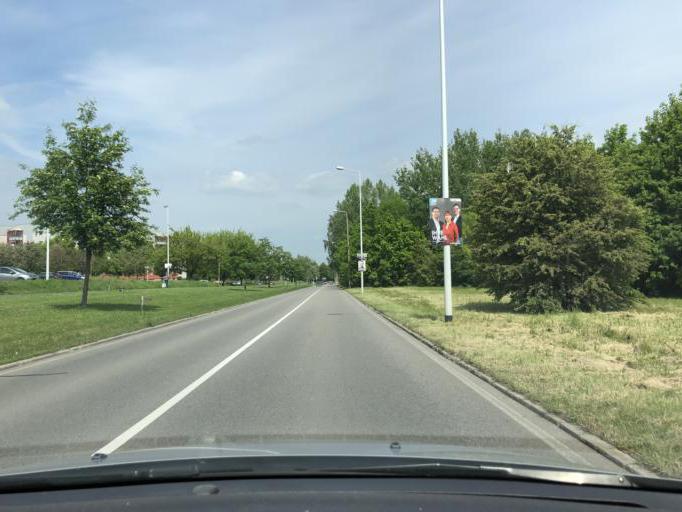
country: DE
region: Thuringia
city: Altenburg
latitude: 50.9973
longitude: 12.4263
